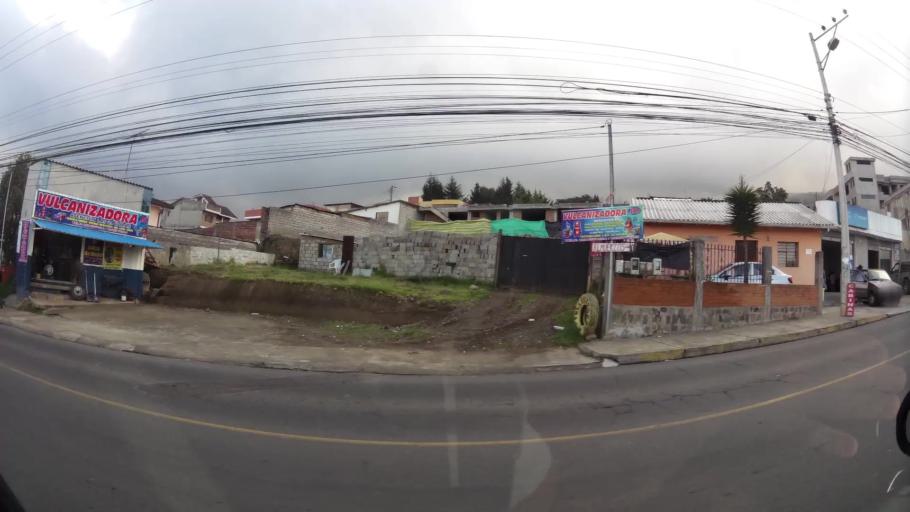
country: EC
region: Pichincha
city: Quito
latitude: -0.2816
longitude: -78.4914
